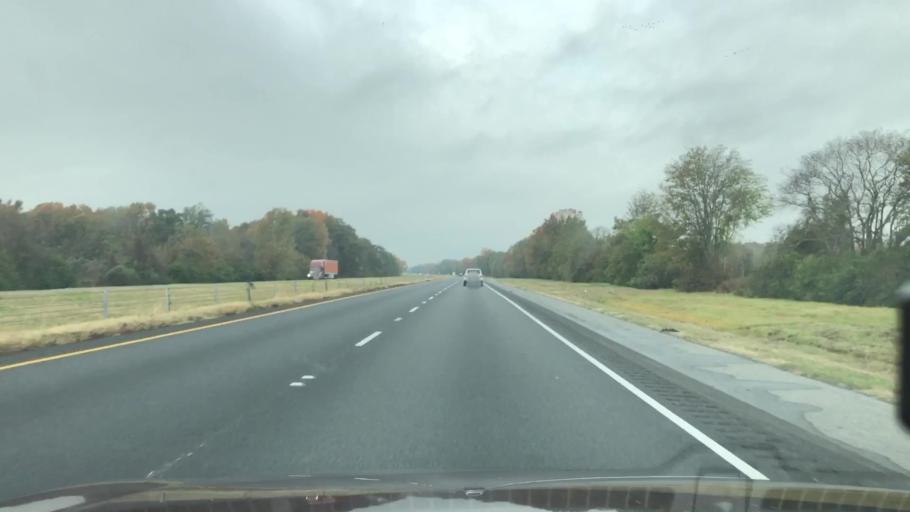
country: US
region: Louisiana
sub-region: Richland Parish
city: Rayville
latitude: 32.4649
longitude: -91.7956
